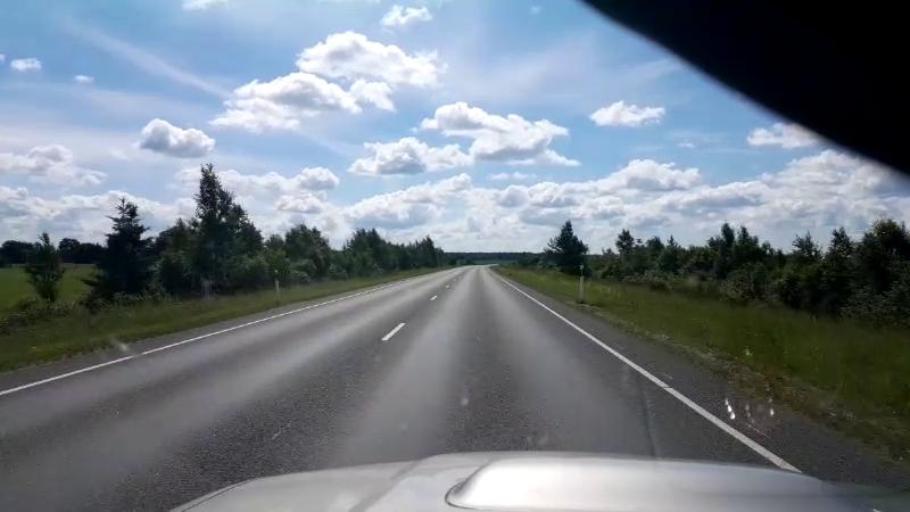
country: EE
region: Jaervamaa
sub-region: Jaerva-Jaani vald
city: Jarva-Jaani
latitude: 59.1542
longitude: 25.7674
